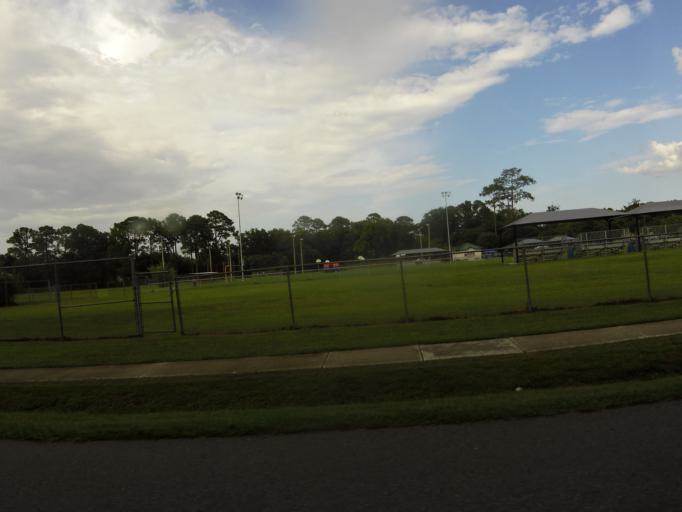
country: US
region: Florida
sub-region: Duval County
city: Jacksonville
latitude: 30.3669
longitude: -81.7111
